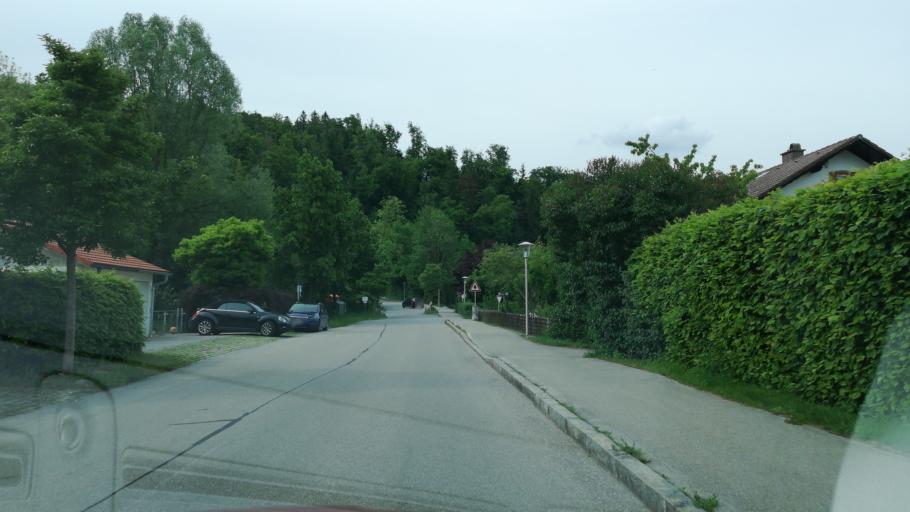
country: DE
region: Bavaria
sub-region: Upper Bavaria
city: Mehring
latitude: 48.1372
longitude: 12.7902
